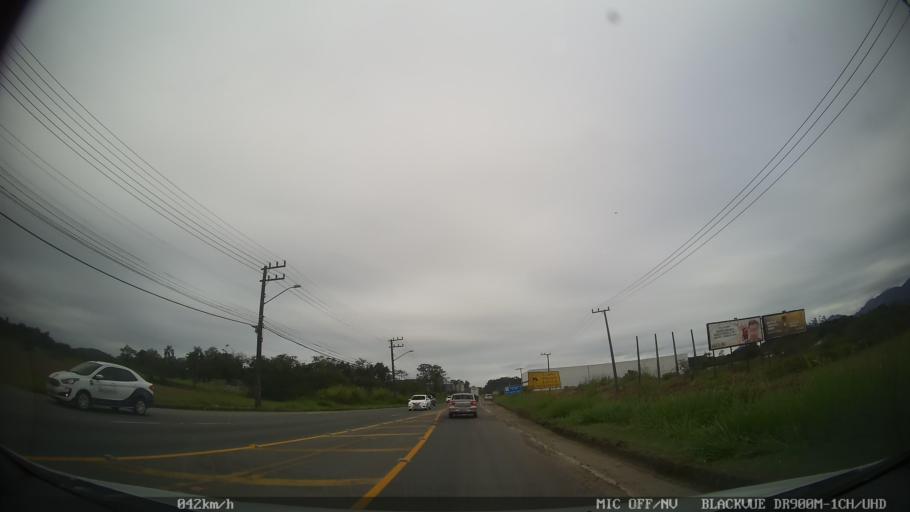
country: BR
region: Santa Catarina
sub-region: Joinville
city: Joinville
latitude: -26.2926
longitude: -48.9203
